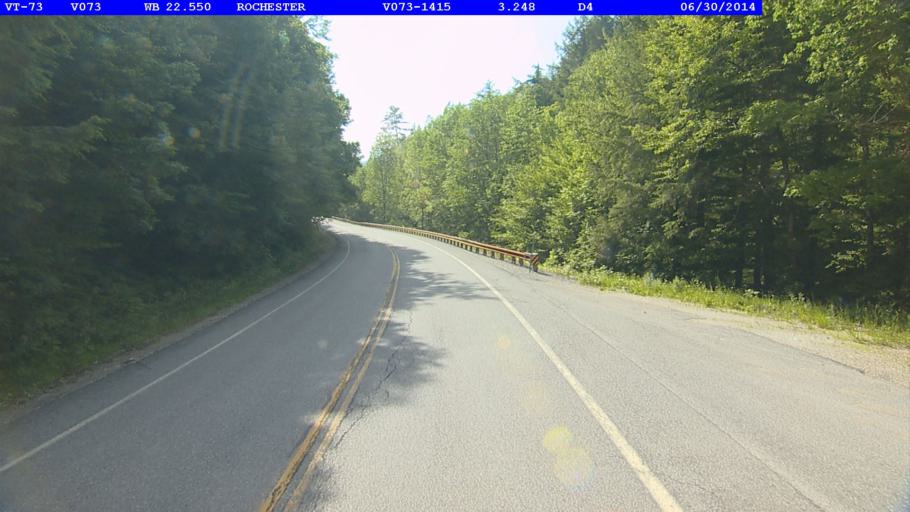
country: US
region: Vermont
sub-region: Rutland County
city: Brandon
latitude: 43.8527
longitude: -72.9059
